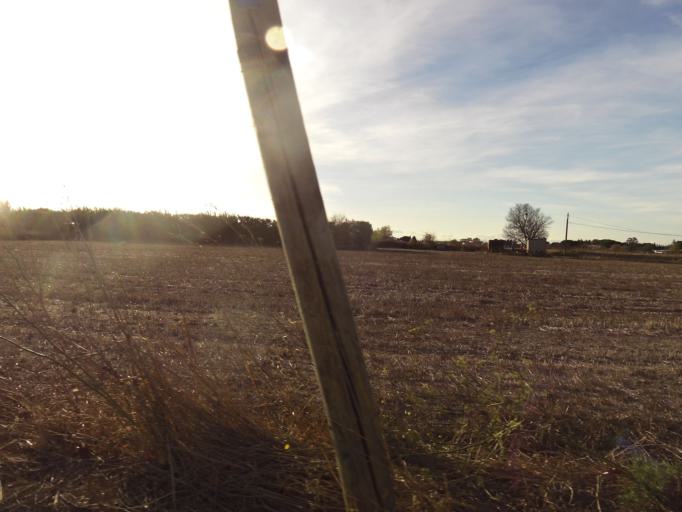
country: FR
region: Languedoc-Roussillon
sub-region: Departement du Gard
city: Aimargues
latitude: 43.6993
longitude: 4.2138
